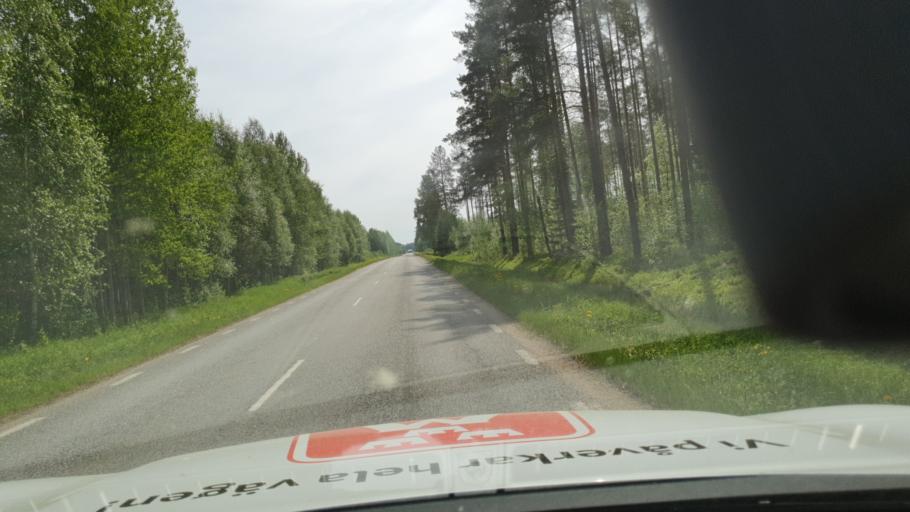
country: SE
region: Vaesterbotten
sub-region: Robertsfors Kommun
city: Robertsfors
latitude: 64.2922
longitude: 20.9020
